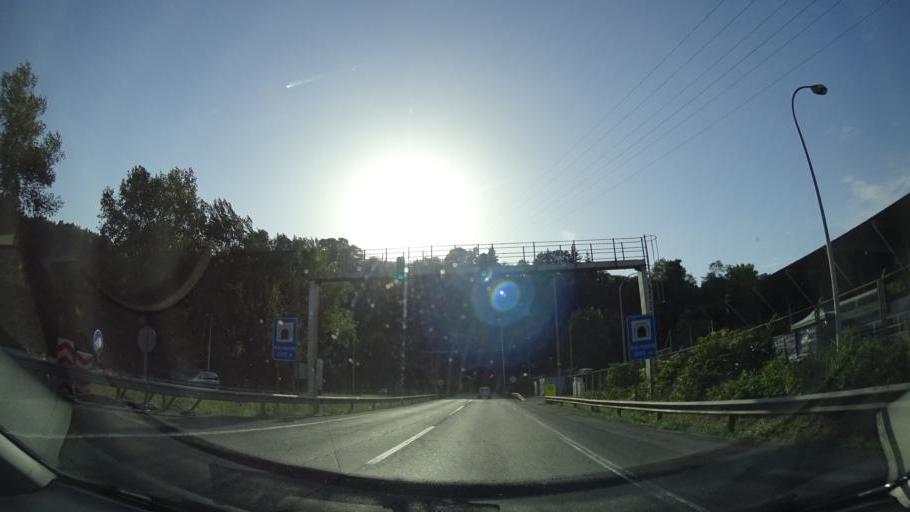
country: ES
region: Basque Country
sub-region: Bizkaia
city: Basauri
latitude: 43.2314
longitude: -2.8893
